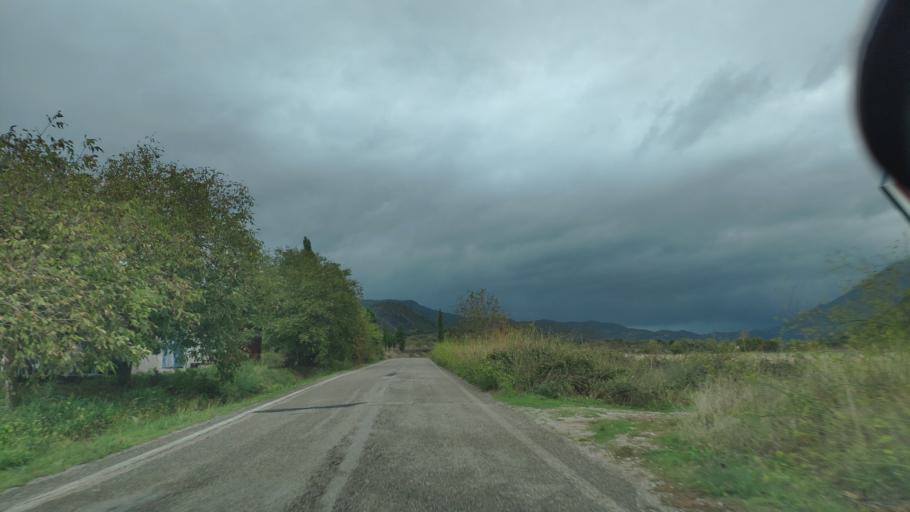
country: GR
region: West Greece
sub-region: Nomos Aitolias kai Akarnanias
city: Krikellos
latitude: 38.9776
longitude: 21.3258
